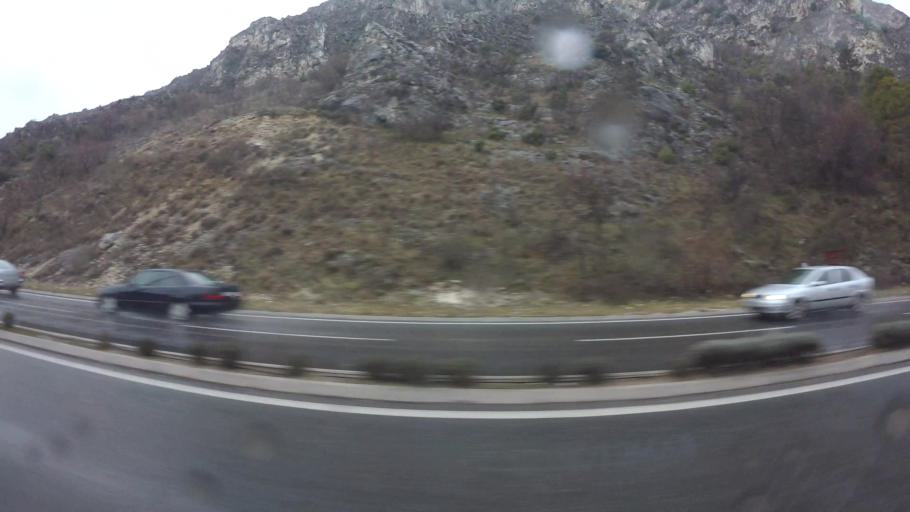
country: BA
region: Federation of Bosnia and Herzegovina
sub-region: Hercegovacko-Bosanski Kanton
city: Mostar
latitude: 43.3286
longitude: 17.8157
